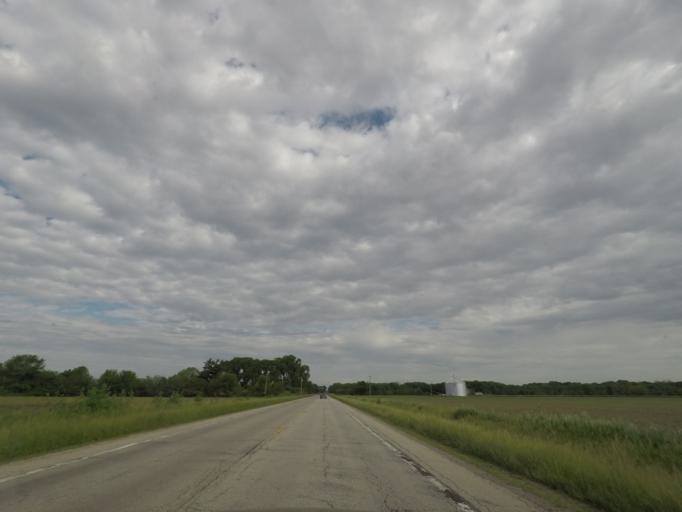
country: US
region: Illinois
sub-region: Logan County
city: Lincoln
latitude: 40.1122
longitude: -89.3289
